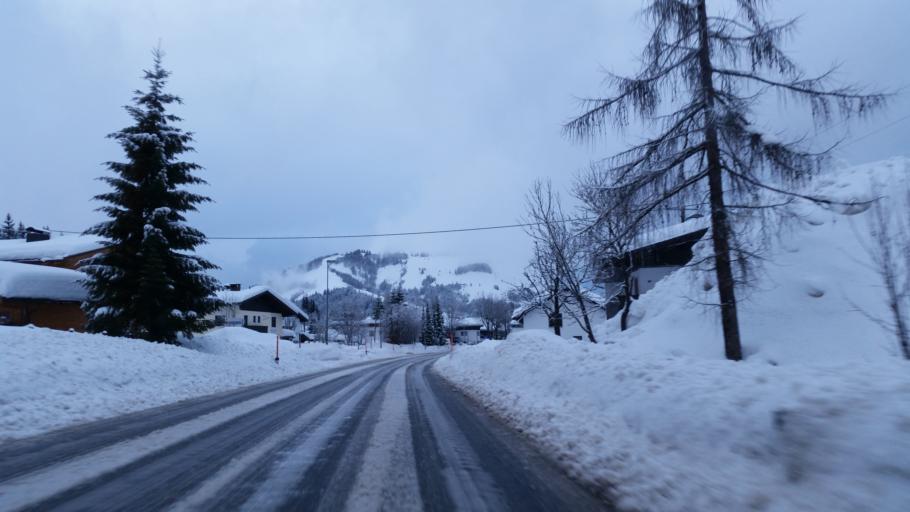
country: AT
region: Tyrol
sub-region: Politischer Bezirk Kitzbuhel
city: Hochfilzen
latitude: 47.4658
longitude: 12.6284
